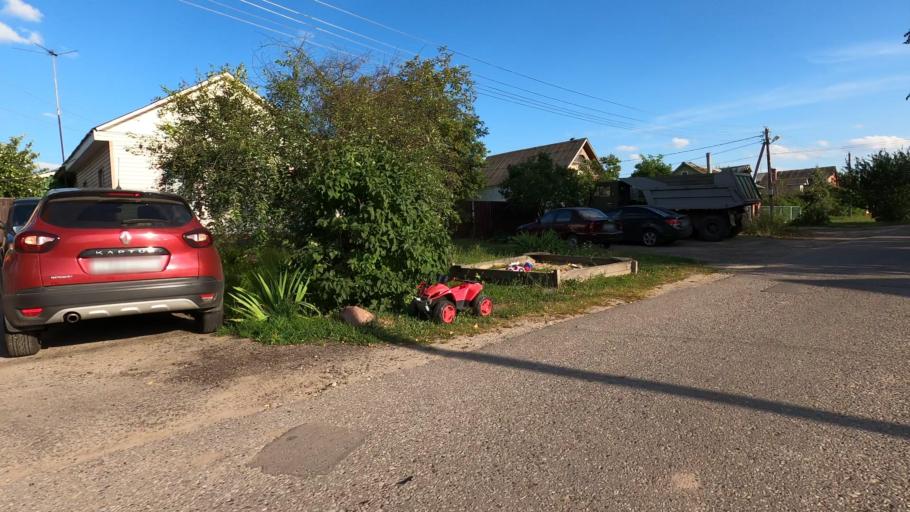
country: RU
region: Moskovskaya
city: Raduzhnyy
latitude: 55.1514
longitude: 38.7370
